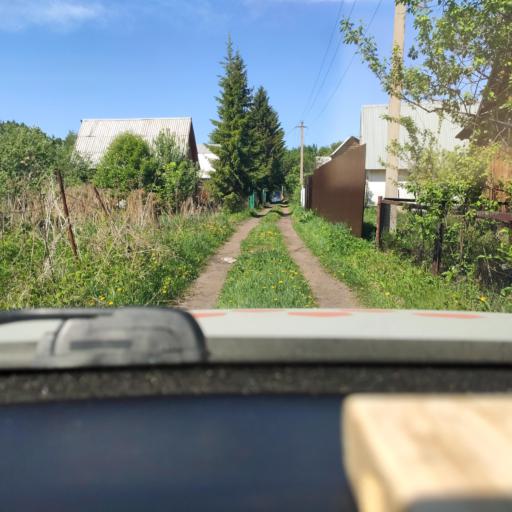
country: RU
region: Bashkortostan
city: Kabakovo
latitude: 54.6635
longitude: 56.1019
